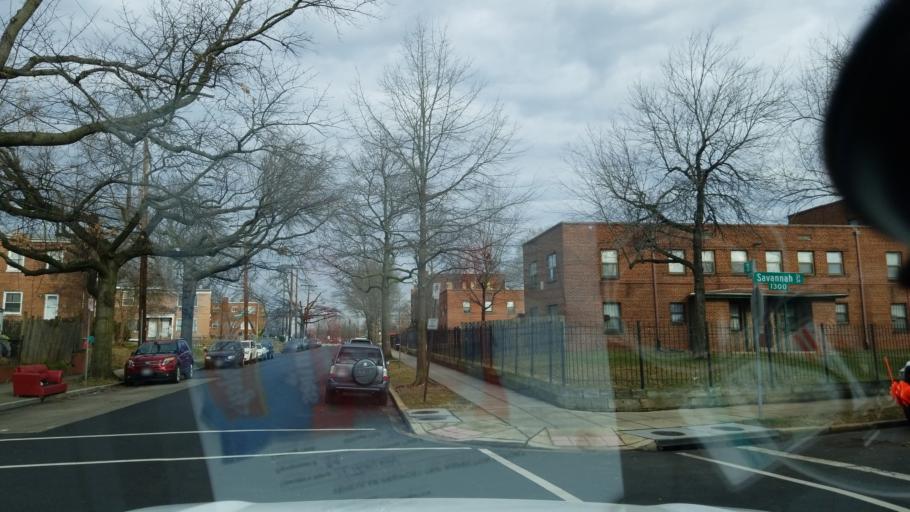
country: US
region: Maryland
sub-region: Prince George's County
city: Glassmanor
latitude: 38.8432
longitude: -76.9885
